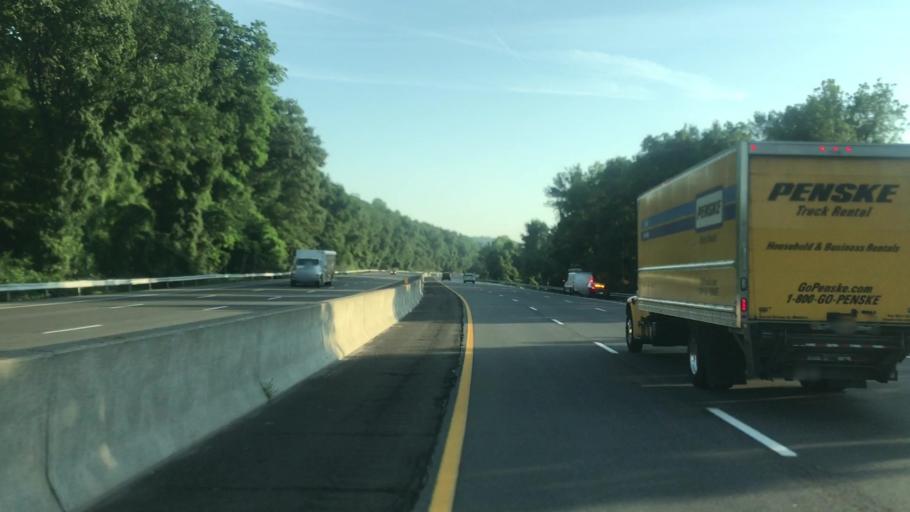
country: US
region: New York
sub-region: Westchester County
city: Ardsley
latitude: 41.0159
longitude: -73.8469
